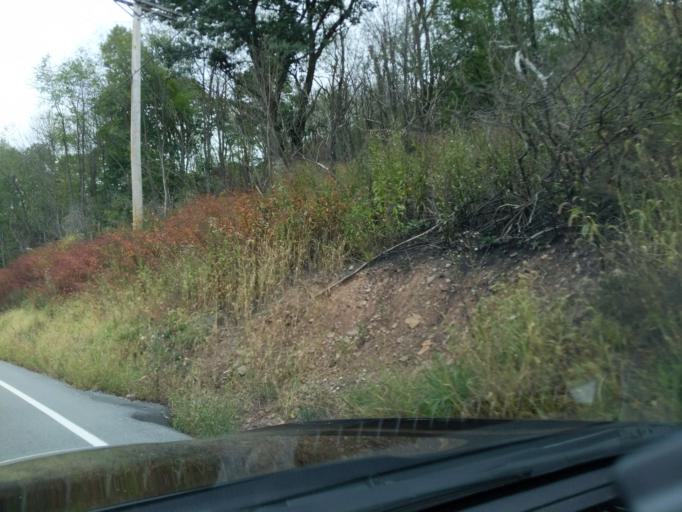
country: US
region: Pennsylvania
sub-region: Cambria County
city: Gallitzin
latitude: 40.4984
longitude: -78.4728
